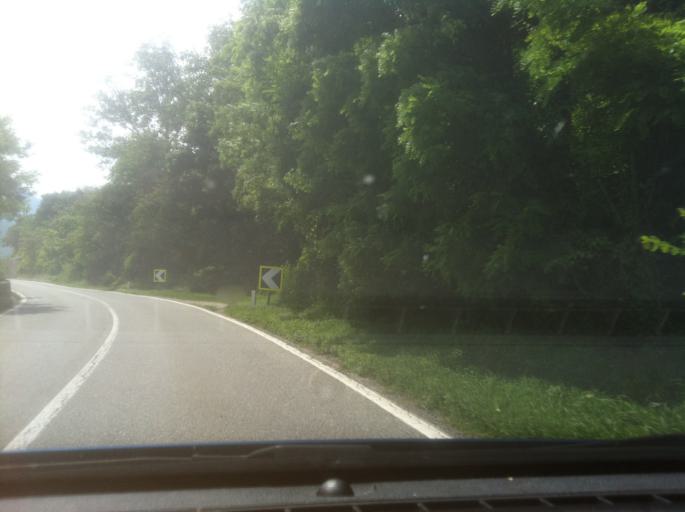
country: IT
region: Aosta Valley
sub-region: Valle d'Aosta
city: Chambave
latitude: 45.7440
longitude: 7.5390
